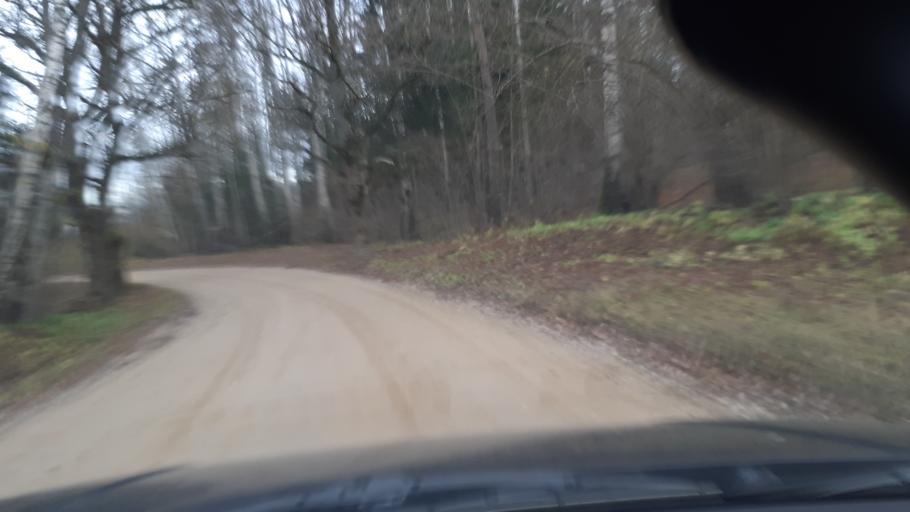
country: LV
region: Alsunga
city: Alsunga
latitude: 56.9764
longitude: 21.6676
